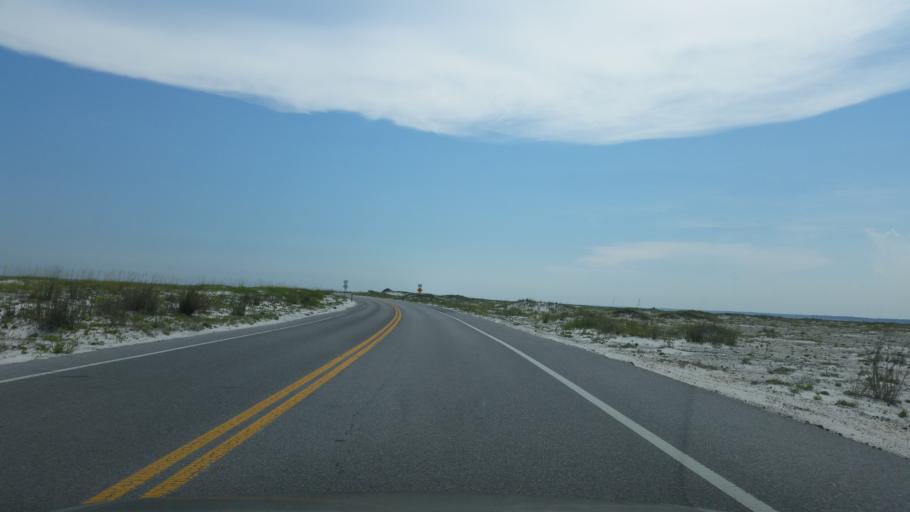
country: US
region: Florida
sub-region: Santa Rosa County
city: Woodlawn Beach
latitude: 30.3706
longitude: -86.9275
